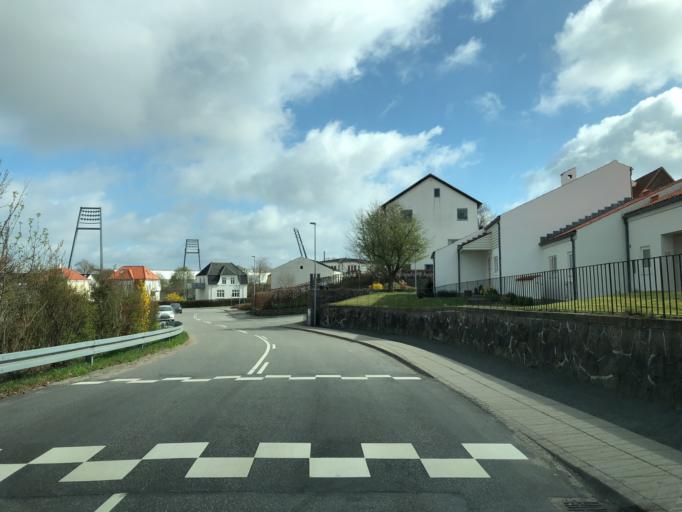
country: DK
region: North Denmark
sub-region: Alborg Kommune
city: Aalborg
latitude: 57.0496
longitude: 9.8950
